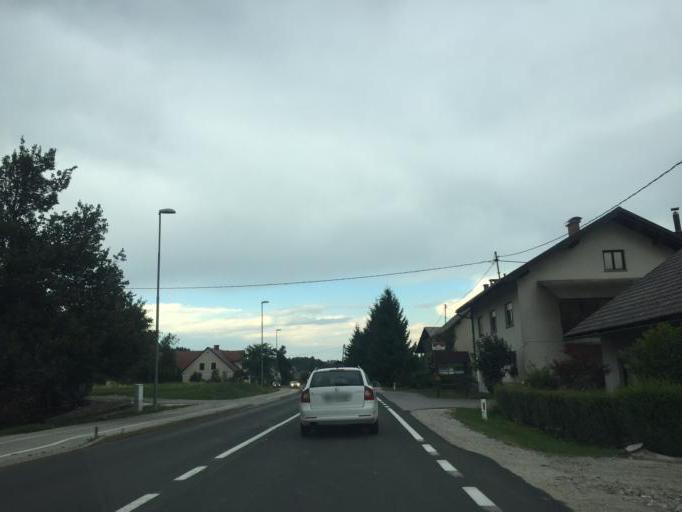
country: SI
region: Logatec
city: Logatec
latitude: 45.9053
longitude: 14.2013
